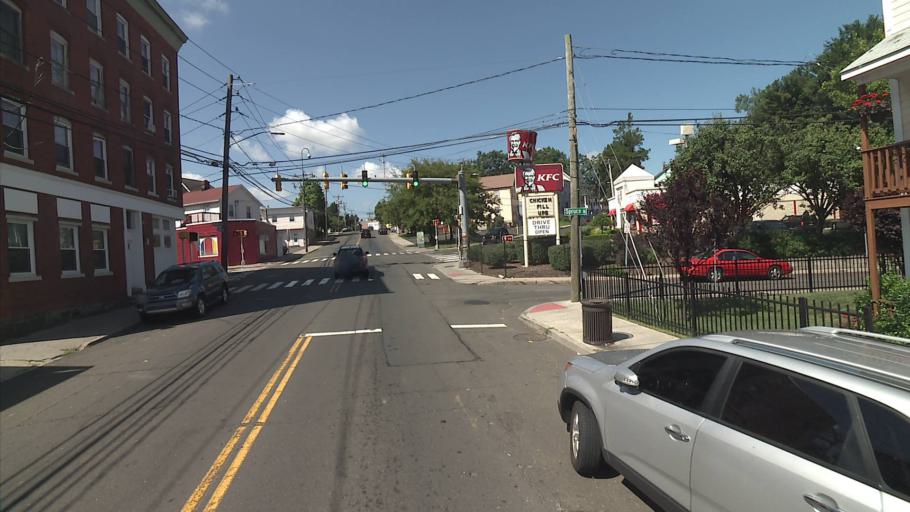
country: US
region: Connecticut
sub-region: Fairfield County
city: Stamford
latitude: 41.0496
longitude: -73.5494
